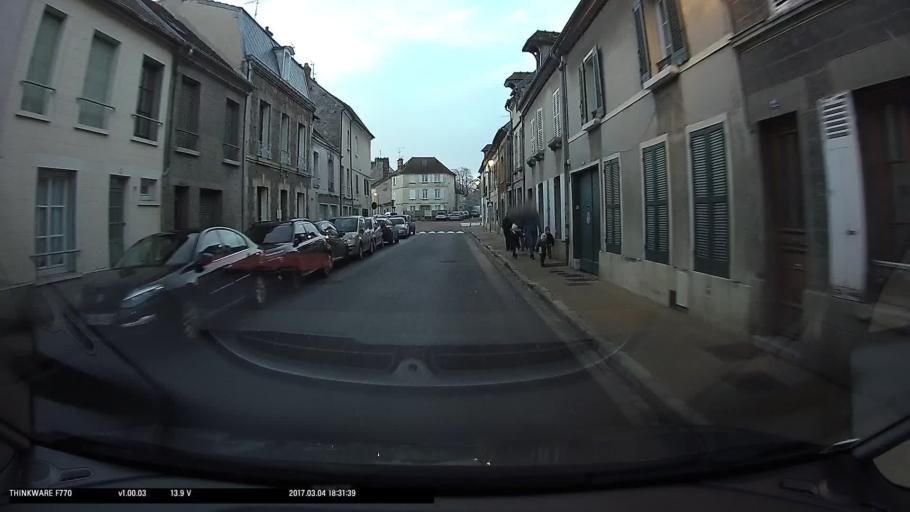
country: FR
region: Ile-de-France
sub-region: Departement du Val-d'Oise
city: Marines
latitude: 49.1451
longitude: 1.9786
